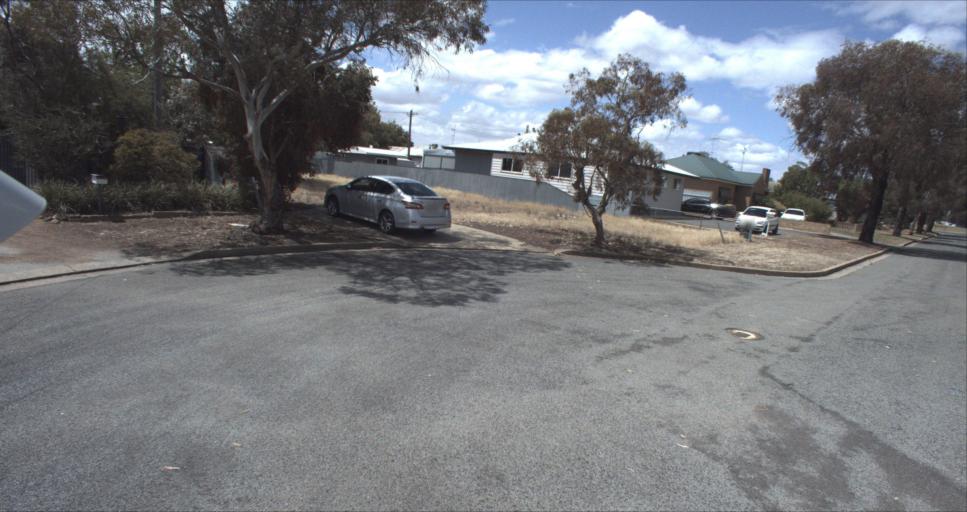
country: AU
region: New South Wales
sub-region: Leeton
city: Leeton
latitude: -34.5599
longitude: 146.3950
